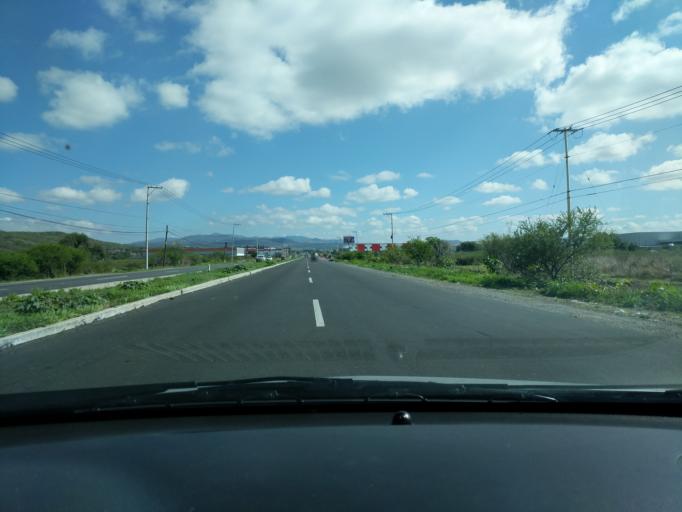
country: MX
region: Queretaro
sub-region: Queretaro
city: Patria Nueva
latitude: 20.6337
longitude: -100.4992
